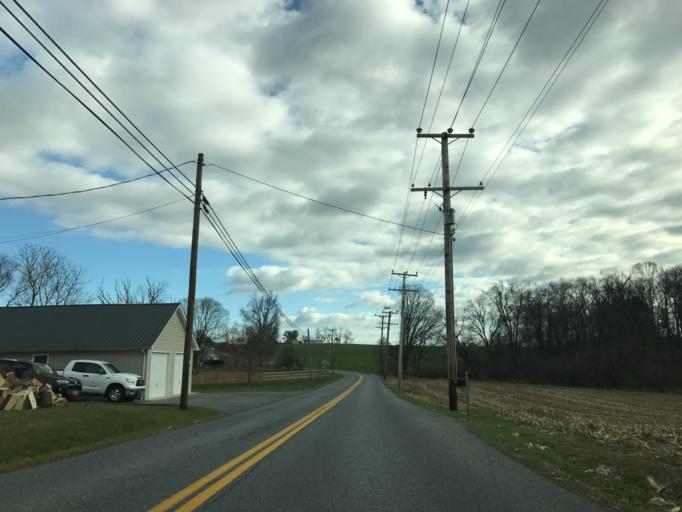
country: US
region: Maryland
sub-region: Harford County
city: Jarrettsville
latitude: 39.6373
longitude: -76.5675
